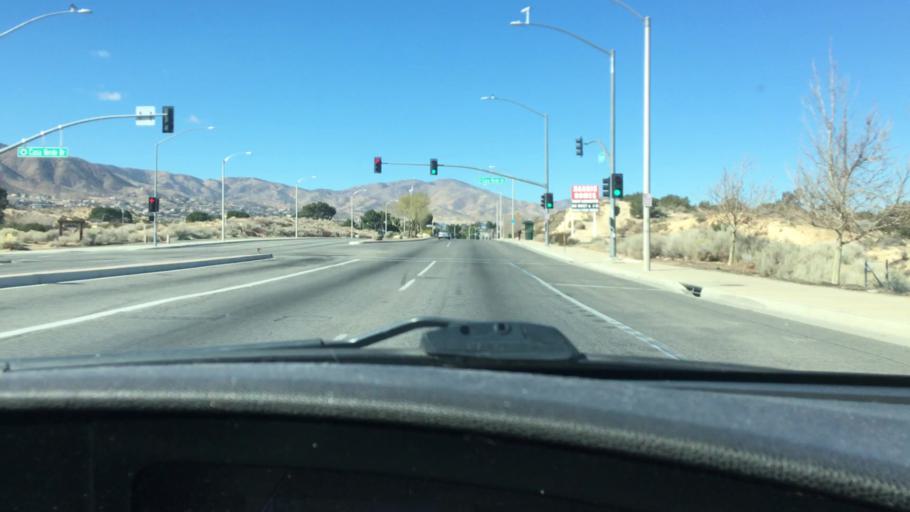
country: US
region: California
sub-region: Los Angeles County
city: Palmdale
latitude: 34.5583
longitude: -118.0998
